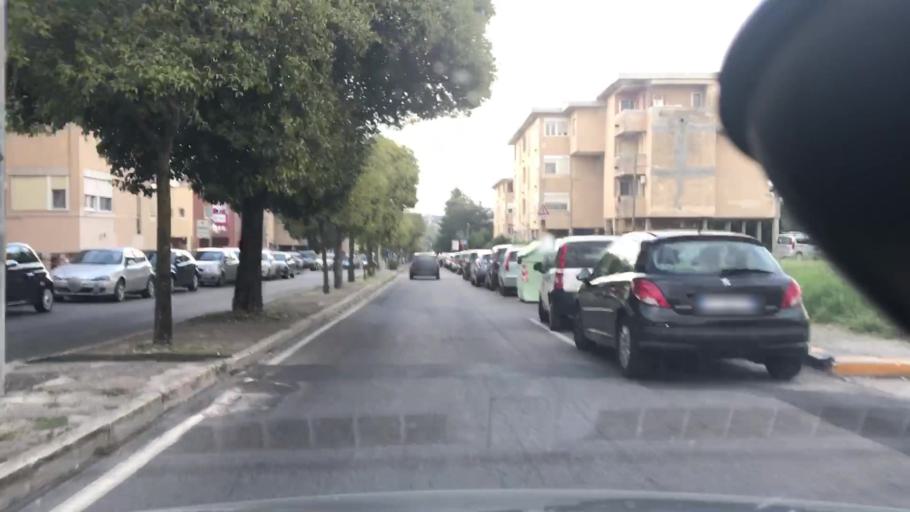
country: IT
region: Basilicate
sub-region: Provincia di Matera
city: Matera
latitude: 40.6837
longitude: 16.5849
